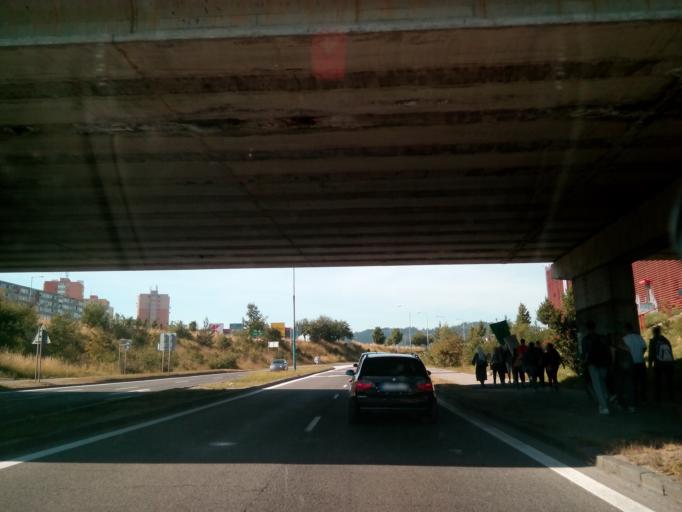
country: SK
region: Presovsky
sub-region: Okres Poprad
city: Poprad
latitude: 49.0472
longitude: 20.2921
